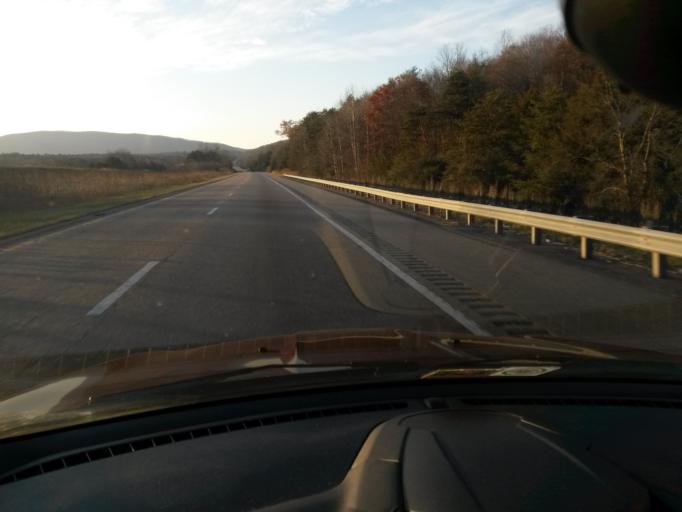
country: US
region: Virginia
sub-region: City of Lexington
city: Lexington
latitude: 37.8680
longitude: -79.5040
